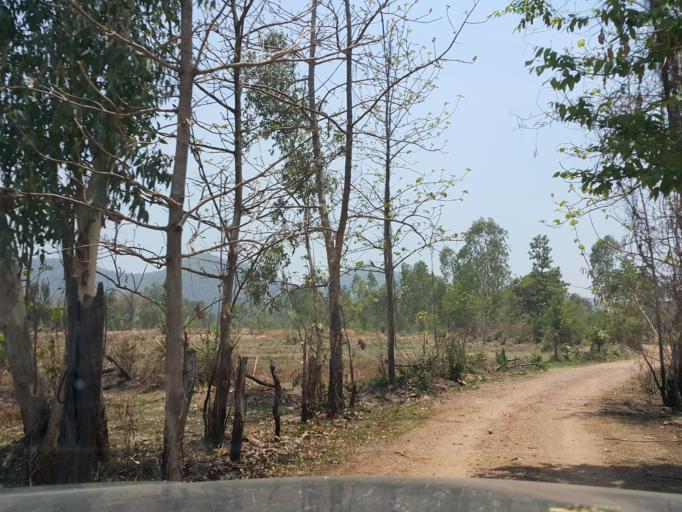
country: TH
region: Lampang
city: Thoen
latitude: 17.6413
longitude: 99.2773
